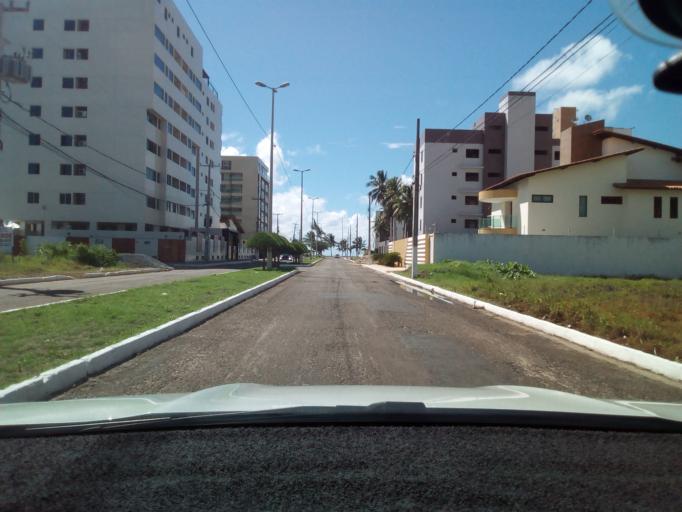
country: BR
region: Paraiba
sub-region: Joao Pessoa
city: Joao Pessoa
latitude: -7.0521
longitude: -34.8449
